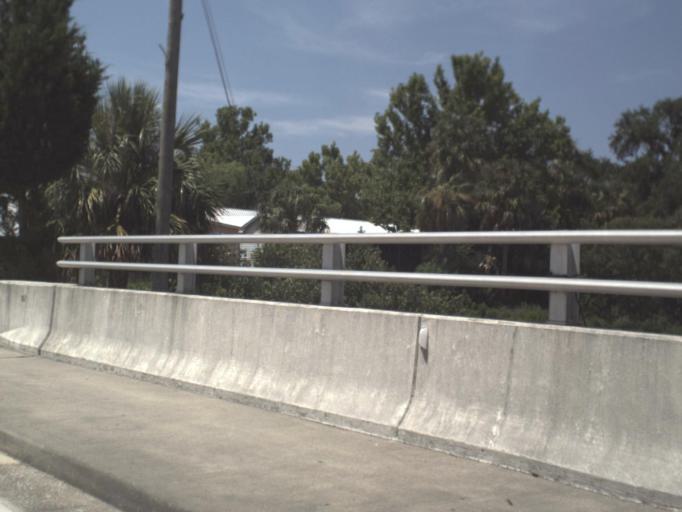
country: US
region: Florida
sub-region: Levy County
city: Chiefland
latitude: 29.1394
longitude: -83.0352
